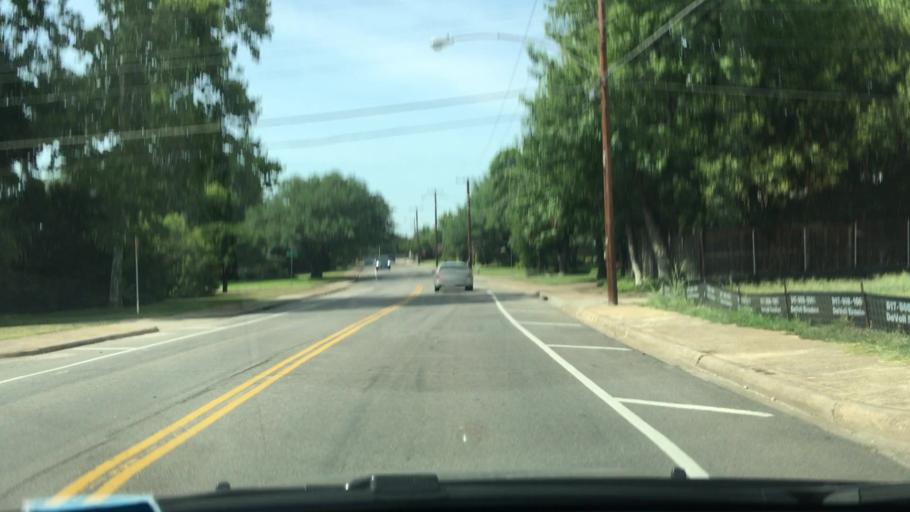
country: US
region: Texas
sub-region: Dallas County
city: Addison
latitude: 32.9158
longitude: -96.8117
